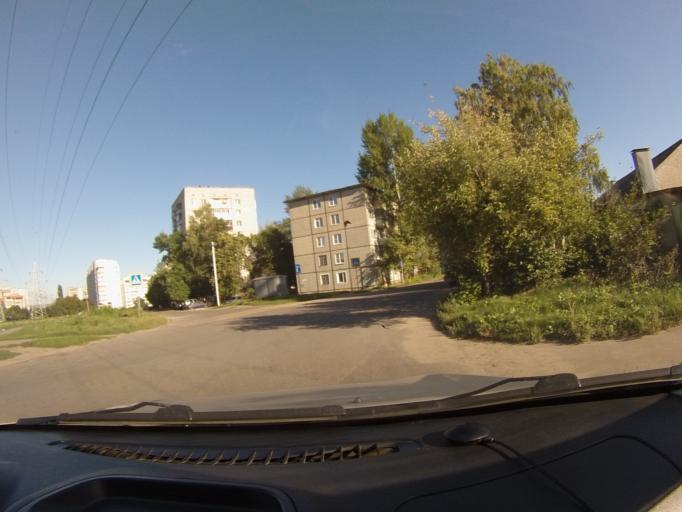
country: RU
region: Tambov
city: Tambov
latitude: 52.7599
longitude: 41.4201
